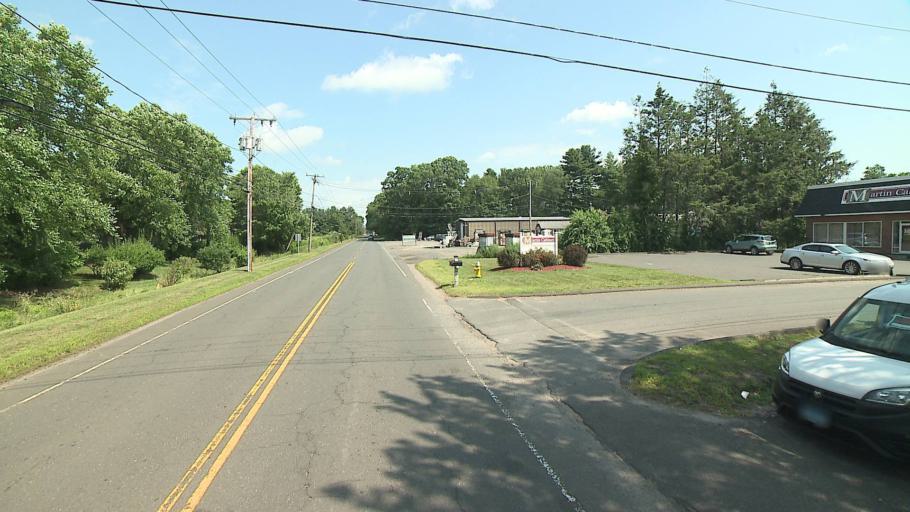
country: US
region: Connecticut
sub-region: Hartford County
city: Plainville
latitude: 41.6525
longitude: -72.8749
